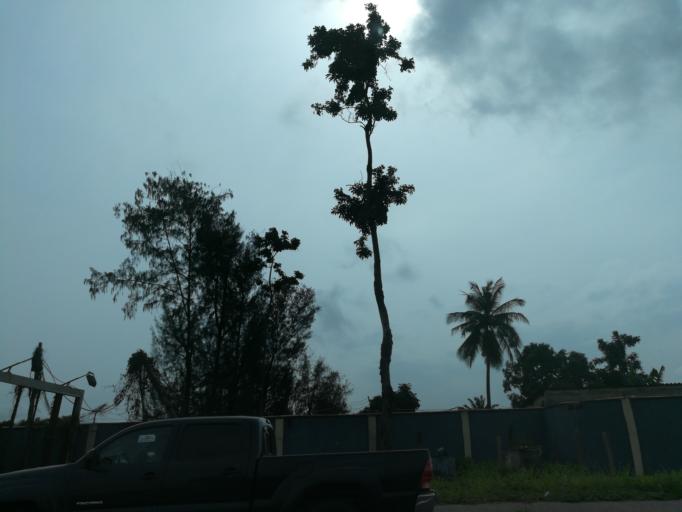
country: NG
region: Lagos
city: Oshodi
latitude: 6.5808
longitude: 3.3340
